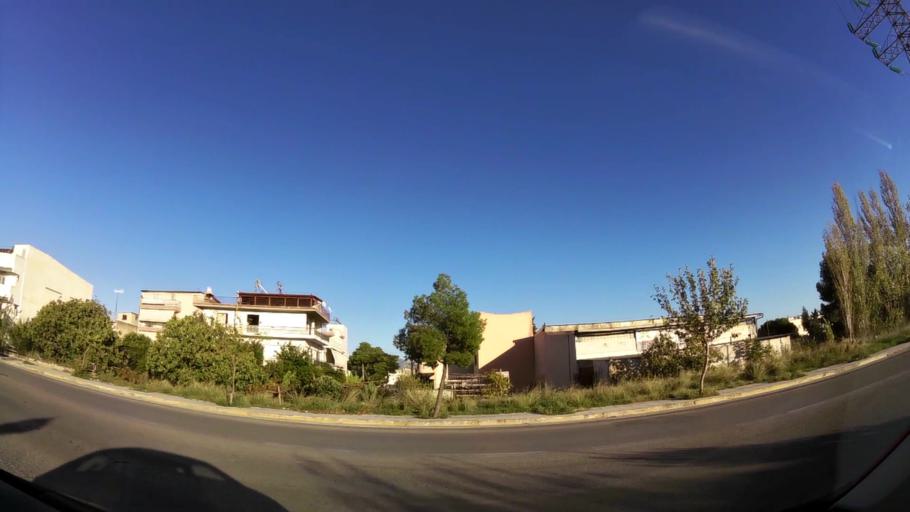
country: GR
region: Attica
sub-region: Nomarchia Anatolikis Attikis
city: Acharnes
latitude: 38.0826
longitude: 23.7259
